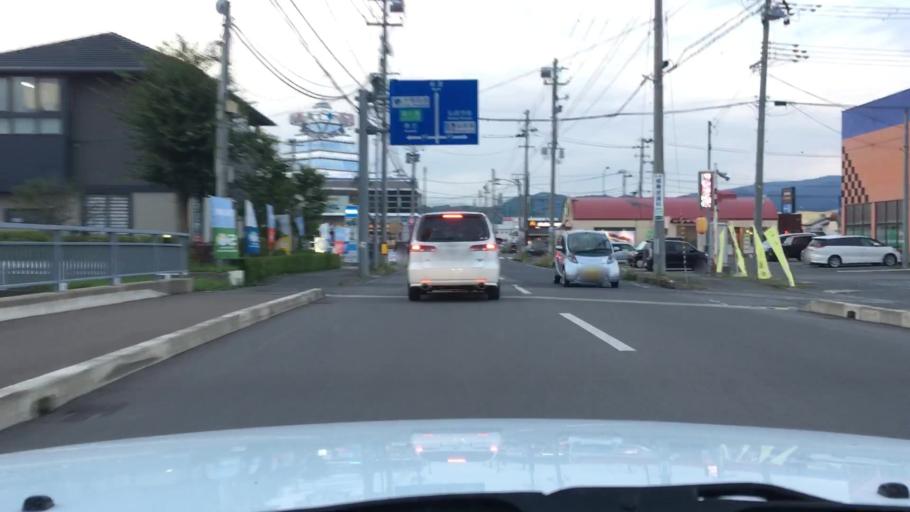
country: JP
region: Aomori
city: Hirosaki
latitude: 40.5980
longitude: 140.5076
